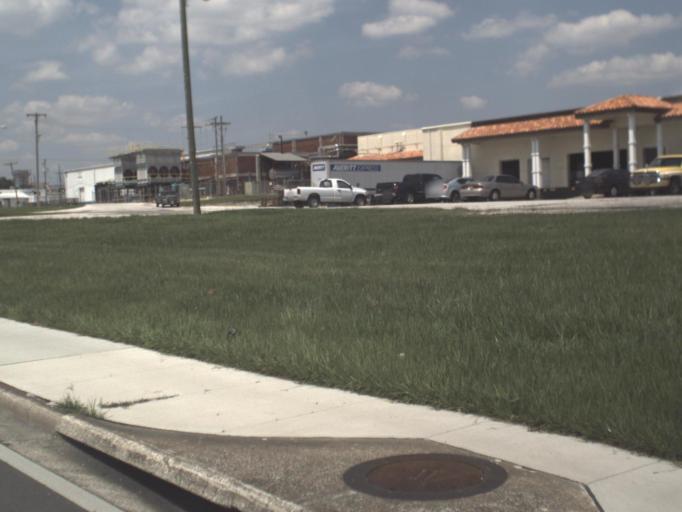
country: US
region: Florida
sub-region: Hillsborough County
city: East Lake-Orient Park
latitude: 27.9563
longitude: -82.4017
